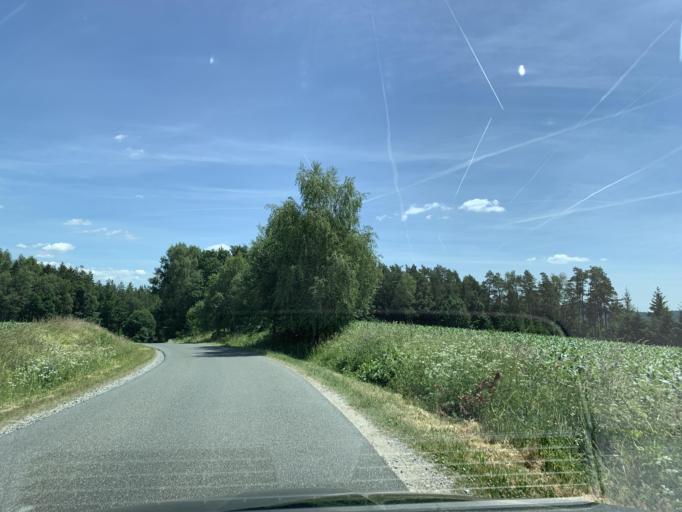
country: DE
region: Bavaria
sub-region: Upper Palatinate
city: Dieterskirchen
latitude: 49.4200
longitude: 12.4021
